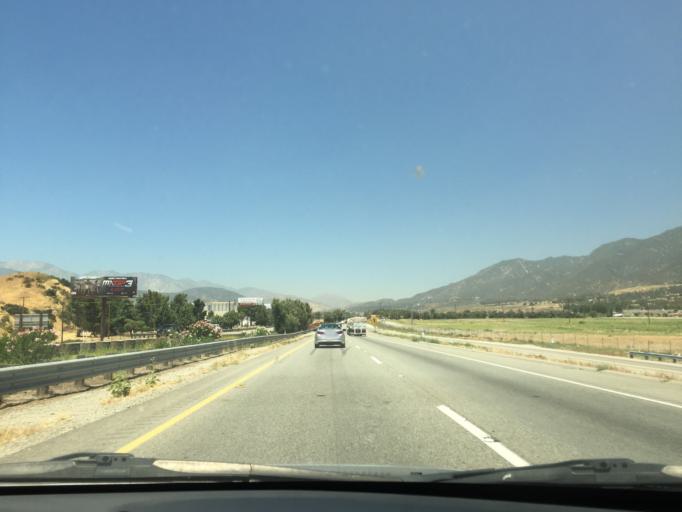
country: US
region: California
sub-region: San Bernardino County
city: Muscoy
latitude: 34.1921
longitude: -117.3628
